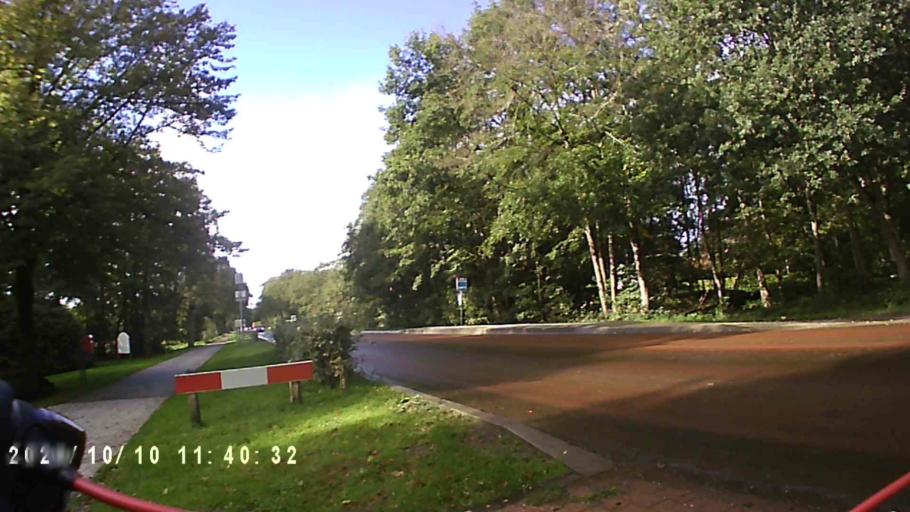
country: NL
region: Friesland
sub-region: Gemeente Smallingerland
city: Drachten
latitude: 53.0666
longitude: 6.1038
